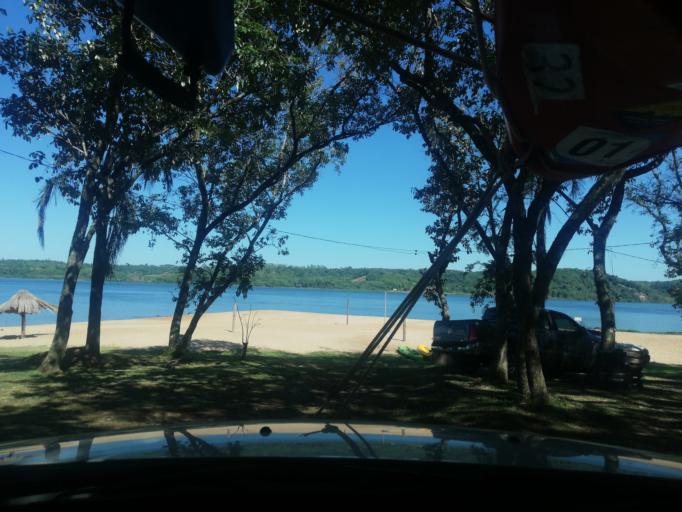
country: AR
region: Misiones
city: Santa Ana
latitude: -27.3310
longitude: -55.5872
